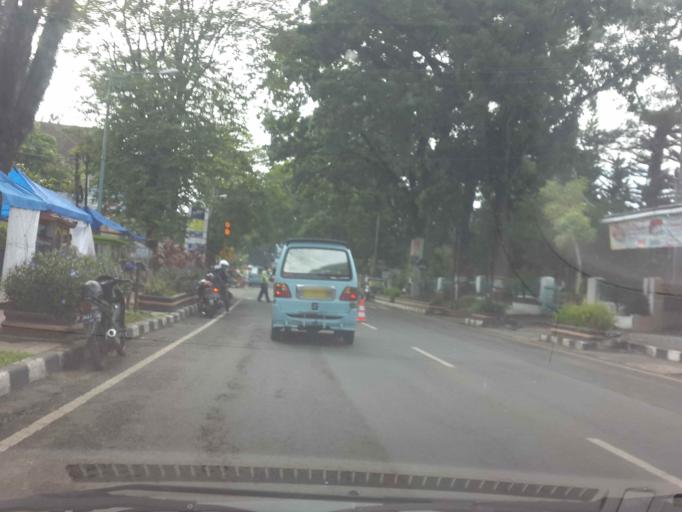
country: ID
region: Central Java
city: Salatiga
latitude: -7.3196
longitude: 110.4981
